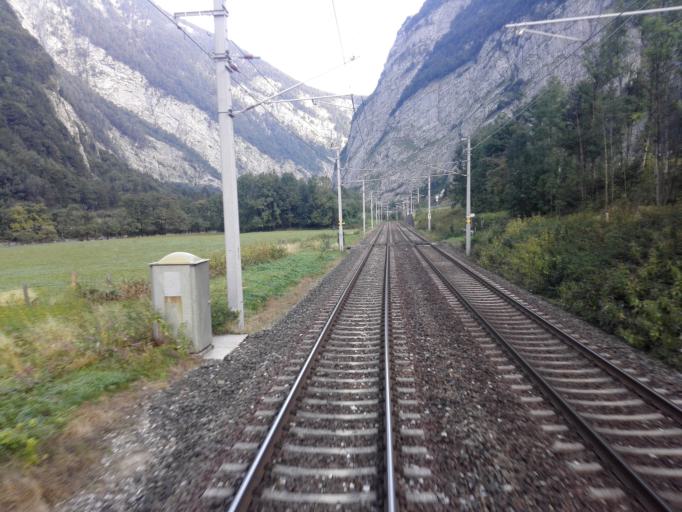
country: AT
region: Salzburg
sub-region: Politischer Bezirk Hallein
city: Golling an der Salzach
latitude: 47.5464
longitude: 13.1698
